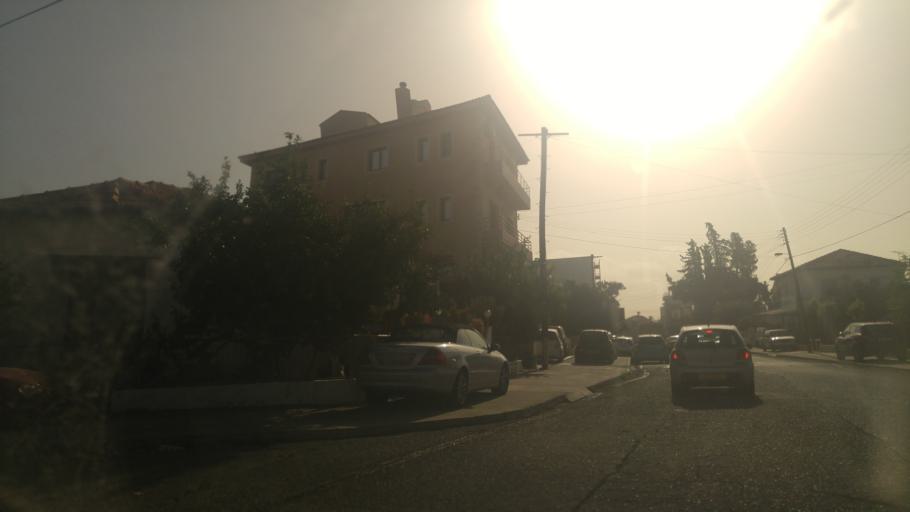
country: CY
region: Limassol
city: Limassol
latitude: 34.6796
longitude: 33.0210
